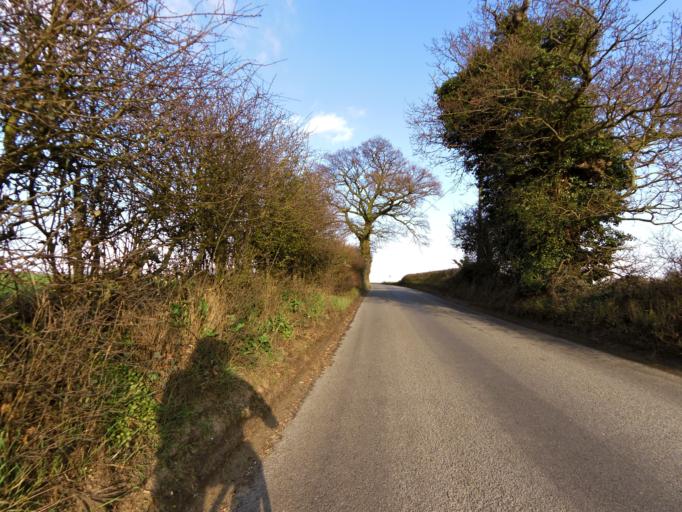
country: GB
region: England
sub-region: Suffolk
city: Kesgrave
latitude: 52.0922
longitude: 1.2271
